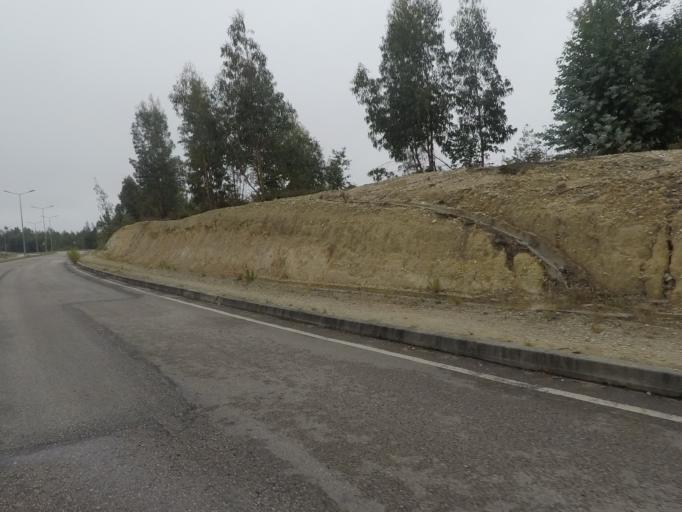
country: PT
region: Coimbra
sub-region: Coimbra
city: Coimbra
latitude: 40.1770
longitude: -8.4611
